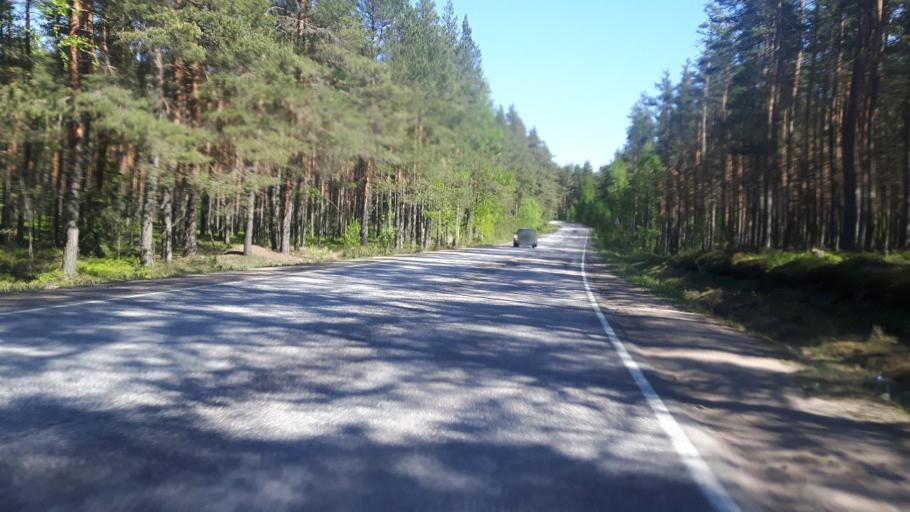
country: RU
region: Leningrad
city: Glebychevo
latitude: 60.2772
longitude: 28.9034
